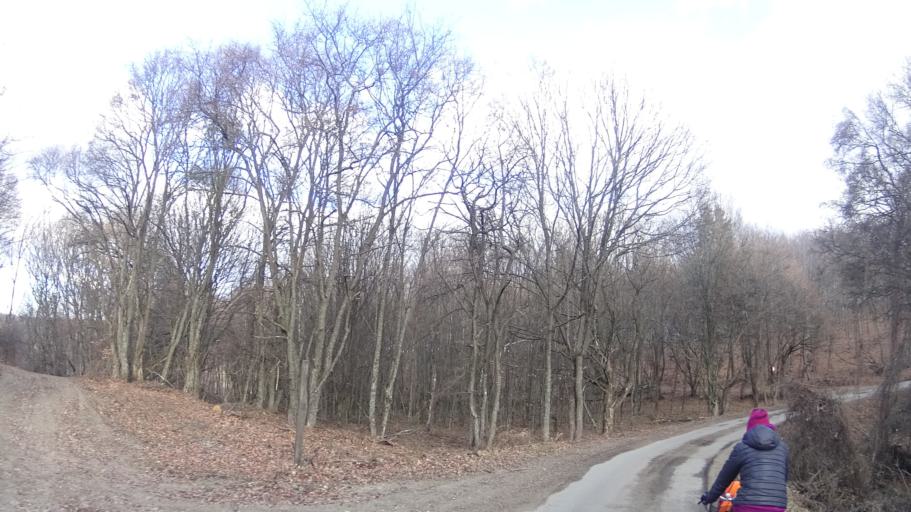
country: HU
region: Heves
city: Szilvasvarad
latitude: 48.0955
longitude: 20.4241
